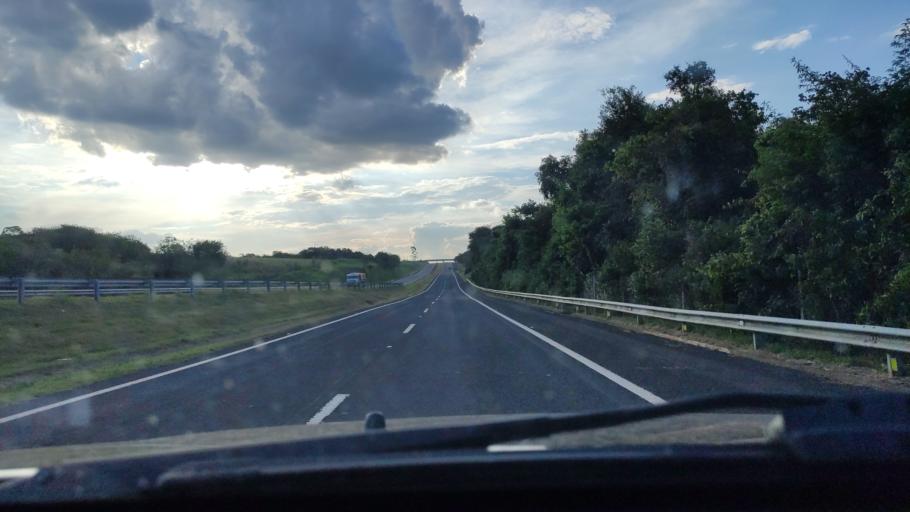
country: BR
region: Sao Paulo
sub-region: Rancharia
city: Rancharia
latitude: -22.4880
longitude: -50.9176
